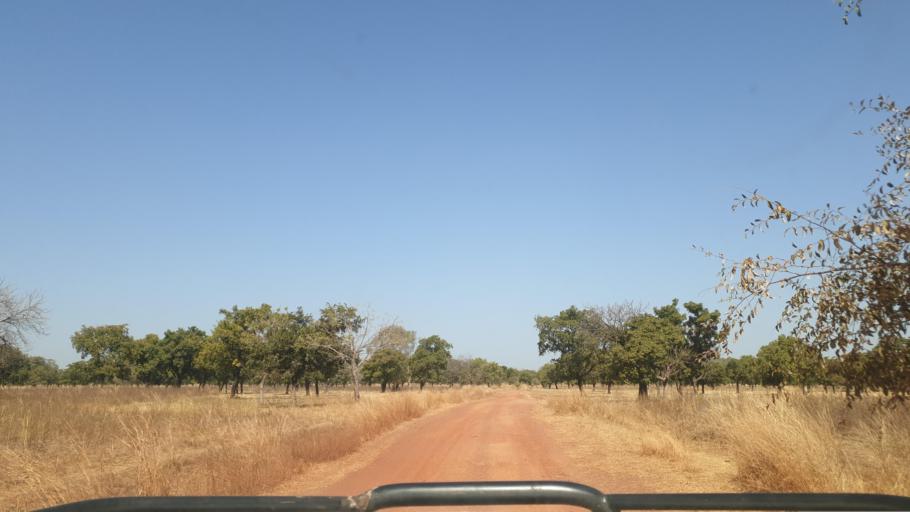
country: ML
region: Koulikoro
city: Dioila
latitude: 11.9000
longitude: -6.9815
